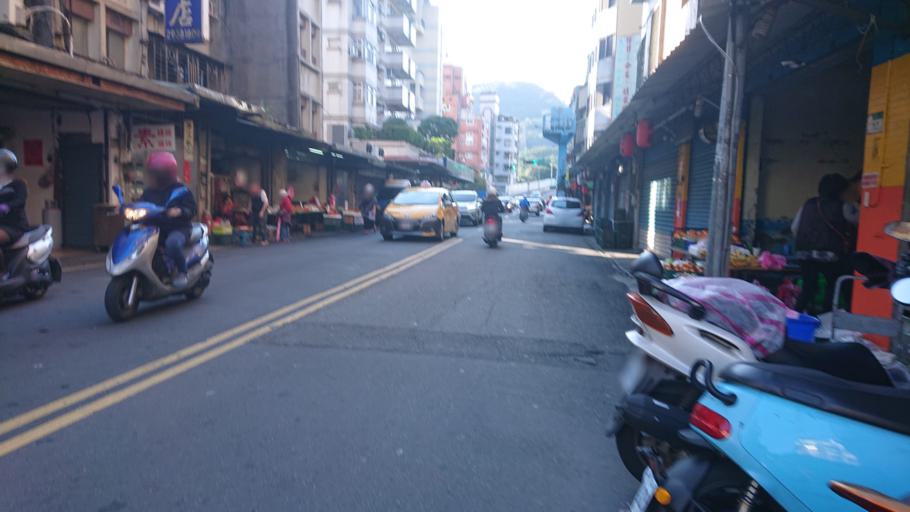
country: TW
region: Taipei
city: Taipei
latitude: 24.9831
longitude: 121.5668
